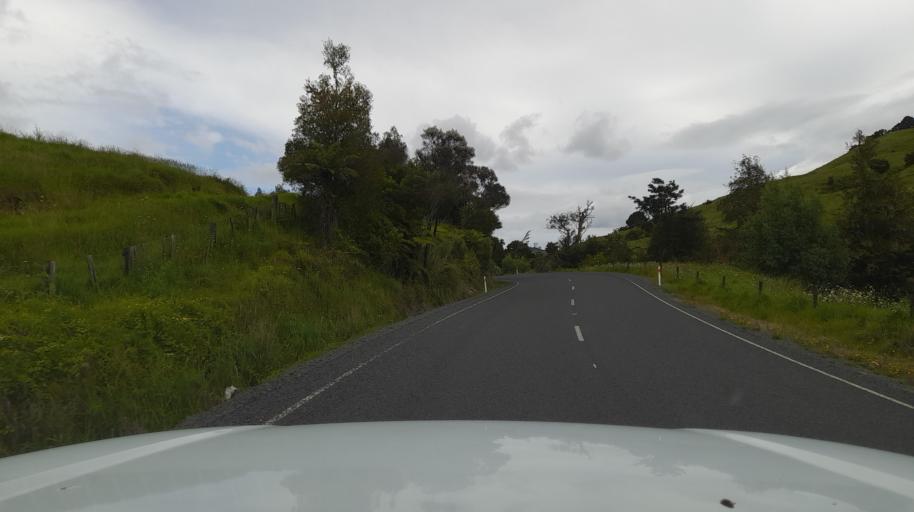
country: NZ
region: Northland
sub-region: Far North District
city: Kaitaia
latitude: -35.3029
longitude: 173.3614
